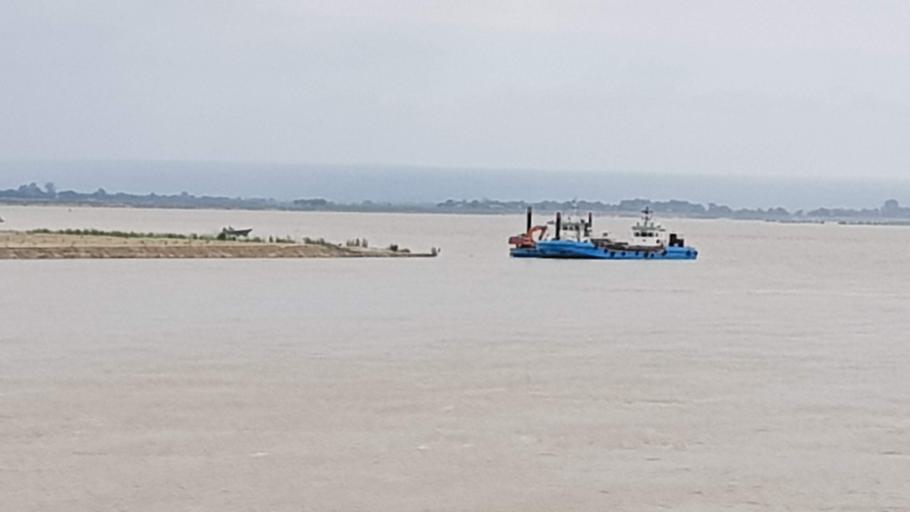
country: MM
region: Magway
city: Pakokku
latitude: 21.4308
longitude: 95.2158
